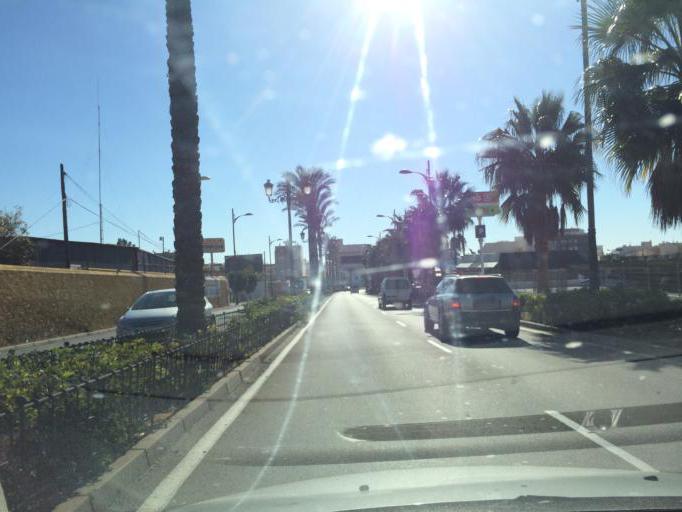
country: ES
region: Andalusia
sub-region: Provincia de Almeria
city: Aguadulce
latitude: 36.8111
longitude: -2.5979
